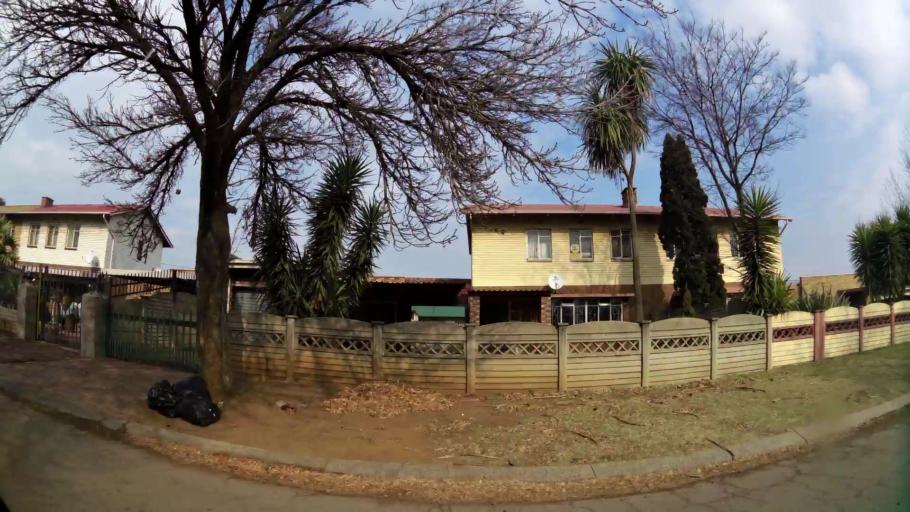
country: ZA
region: Gauteng
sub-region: Sedibeng District Municipality
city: Vanderbijlpark
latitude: -26.6899
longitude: 27.8382
